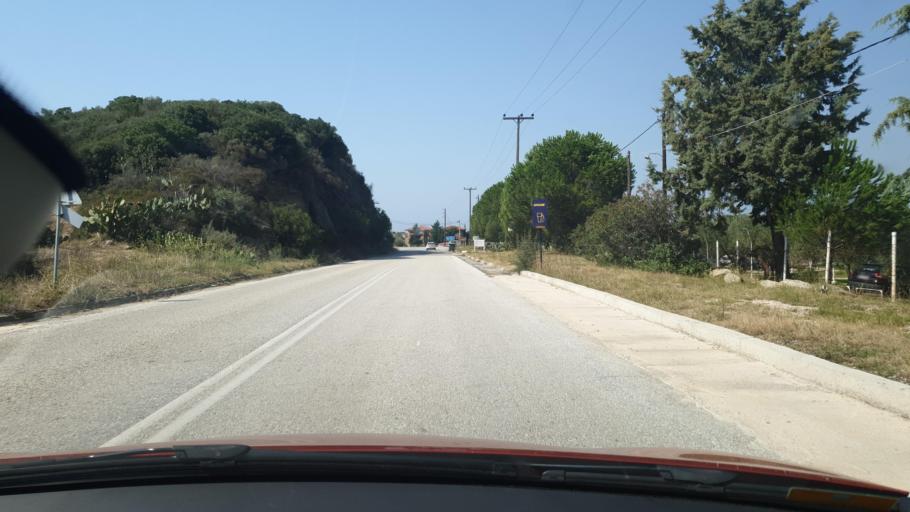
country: GR
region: Central Macedonia
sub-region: Nomos Chalkidikis
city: Sykia
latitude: 39.9859
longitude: 23.9117
